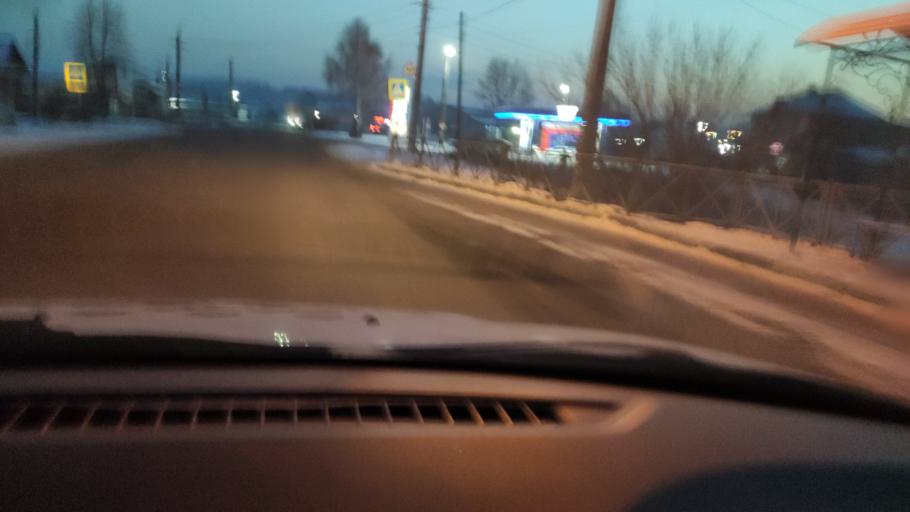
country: RU
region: Perm
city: Kungur
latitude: 57.4265
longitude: 56.9319
